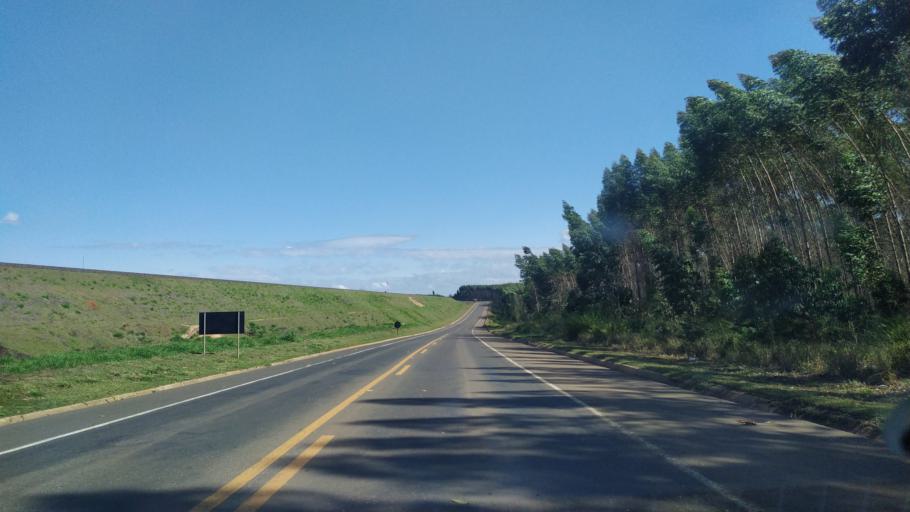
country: BR
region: Parana
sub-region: Telemaco Borba
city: Telemaco Borba
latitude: -24.2410
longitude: -50.7670
